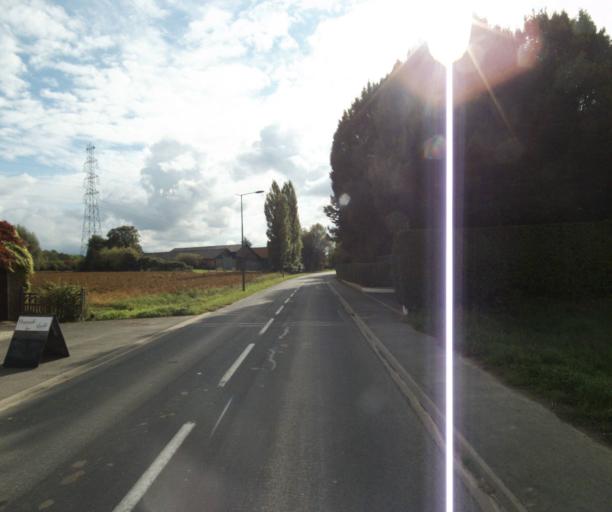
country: FR
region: Nord-Pas-de-Calais
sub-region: Departement du Nord
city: Premesques
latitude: 50.6521
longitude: 2.9501
